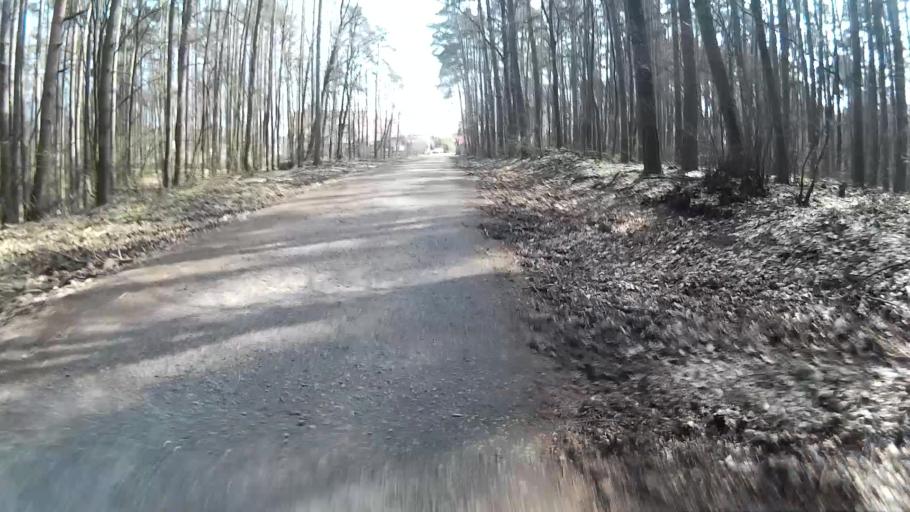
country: CZ
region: South Moravian
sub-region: Mesto Brno
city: Mokra Hora
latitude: 49.2596
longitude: 16.6157
